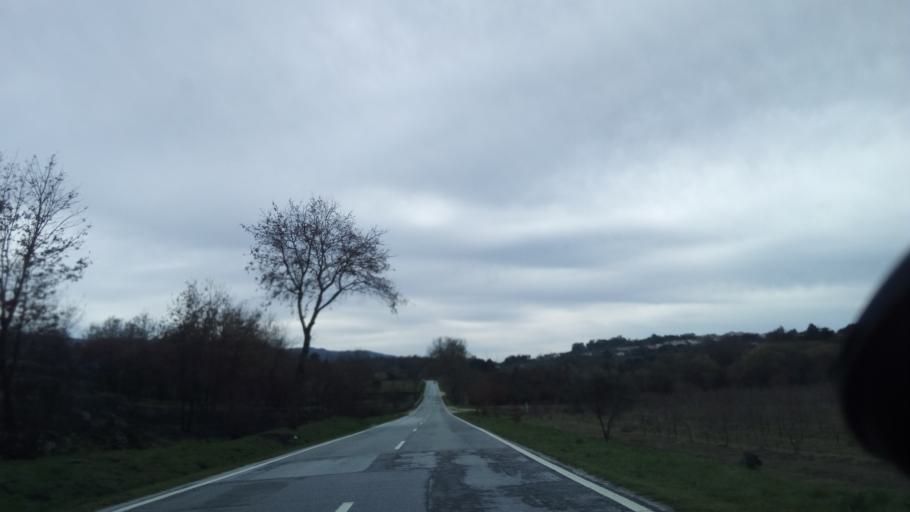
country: PT
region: Guarda
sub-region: Seia
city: Seia
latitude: 40.4975
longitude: -7.6552
